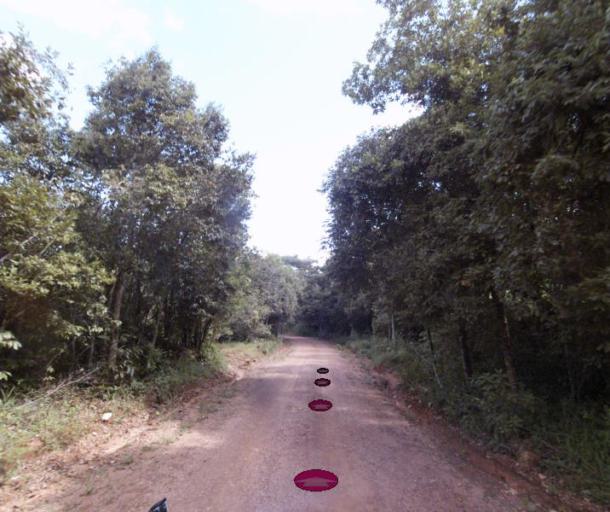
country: BR
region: Goias
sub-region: Pirenopolis
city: Pirenopolis
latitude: -15.7794
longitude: -48.9420
